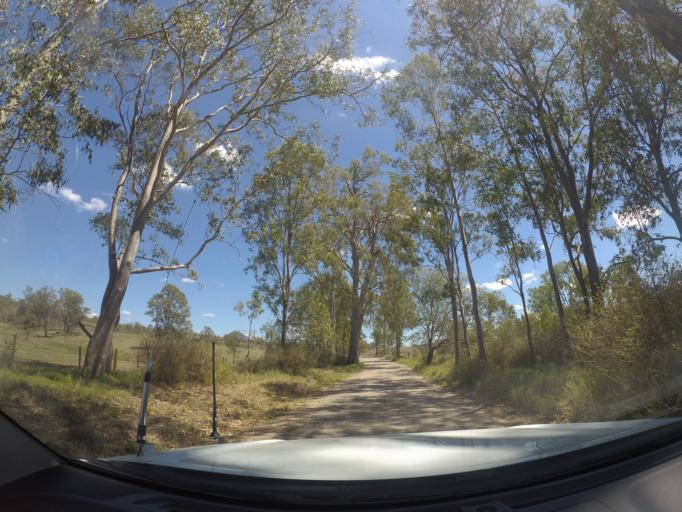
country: AU
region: Queensland
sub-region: Logan
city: Cedar Vale
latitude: -27.8434
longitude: 152.8791
